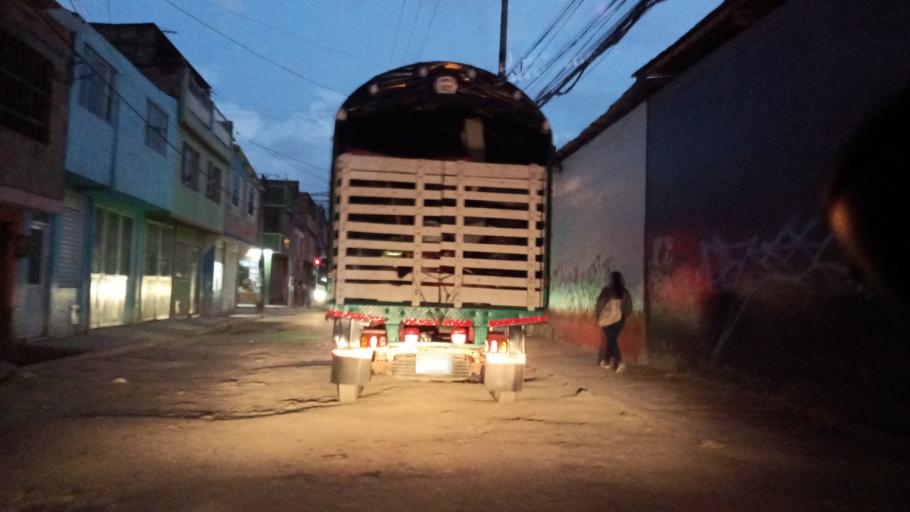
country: CO
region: Cundinamarca
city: Soacha
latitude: 4.5684
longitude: -74.2316
